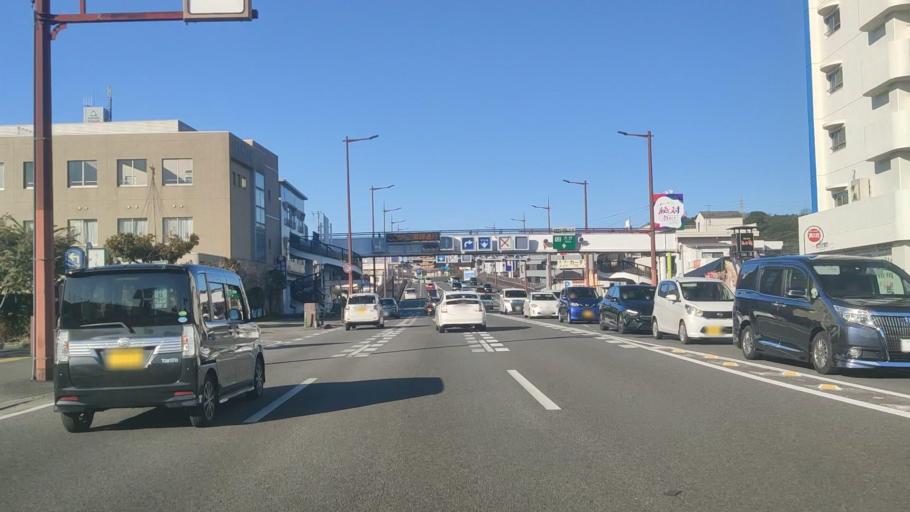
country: JP
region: Oita
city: Oita
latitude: 33.2149
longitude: 131.5958
